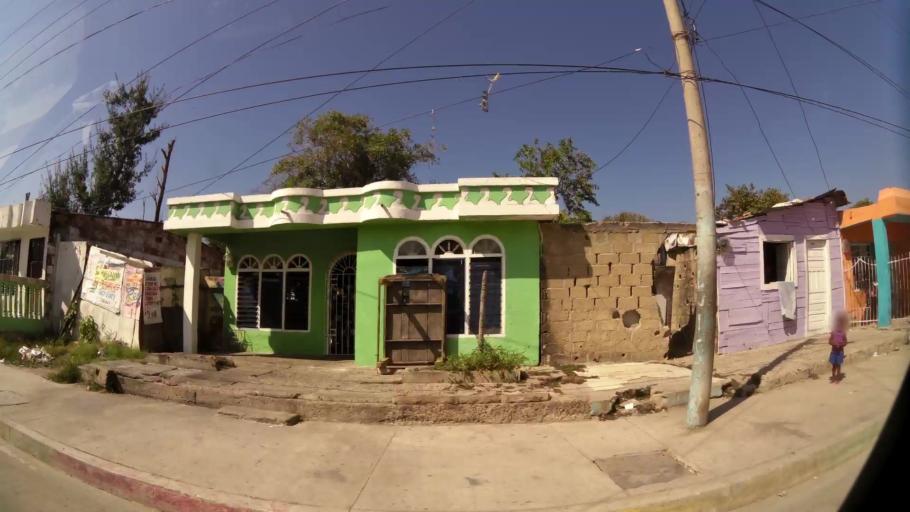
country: CO
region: Bolivar
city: Cartagena
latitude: 10.4141
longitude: -75.5174
